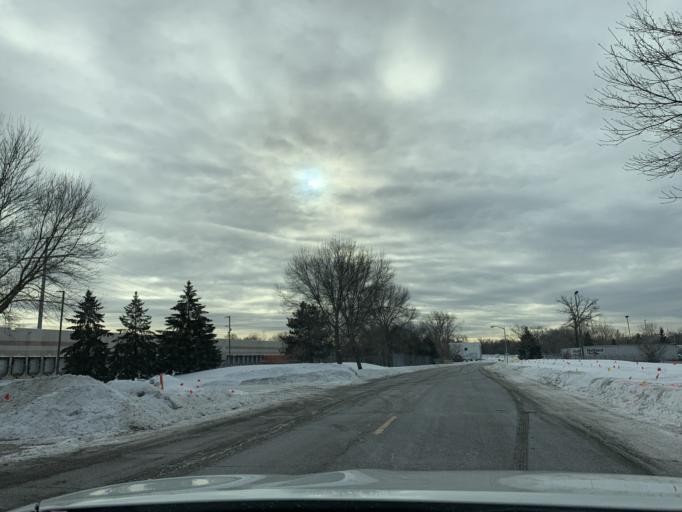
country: US
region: Minnesota
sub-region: Hennepin County
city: West Coon Rapids
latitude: 45.1756
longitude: -93.2971
